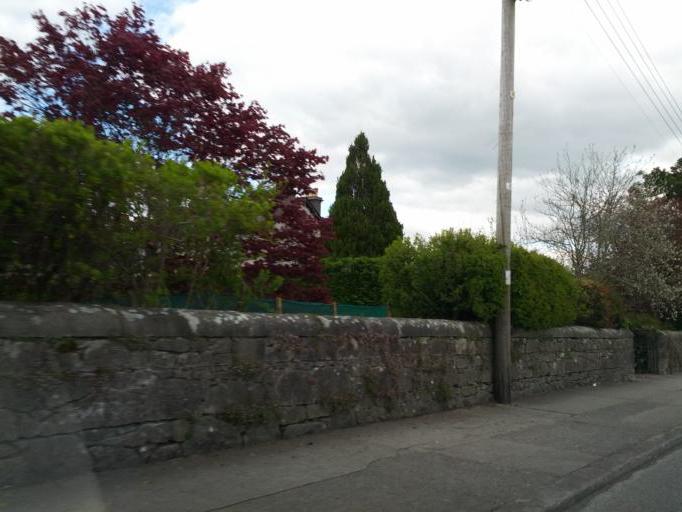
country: IE
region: Connaught
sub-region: County Galway
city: Ballinasloe
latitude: 53.3325
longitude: -8.2327
